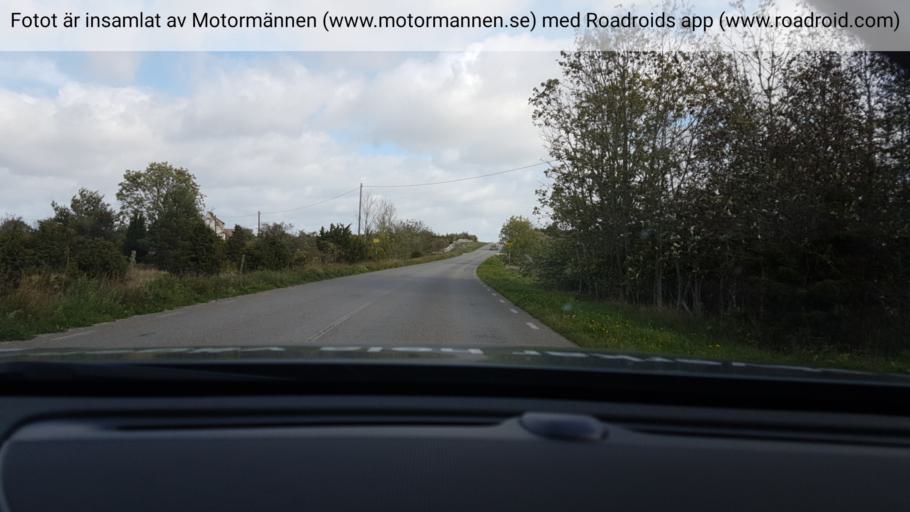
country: SE
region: Gotland
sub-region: Gotland
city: Slite
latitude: 57.9270
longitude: 19.1458
